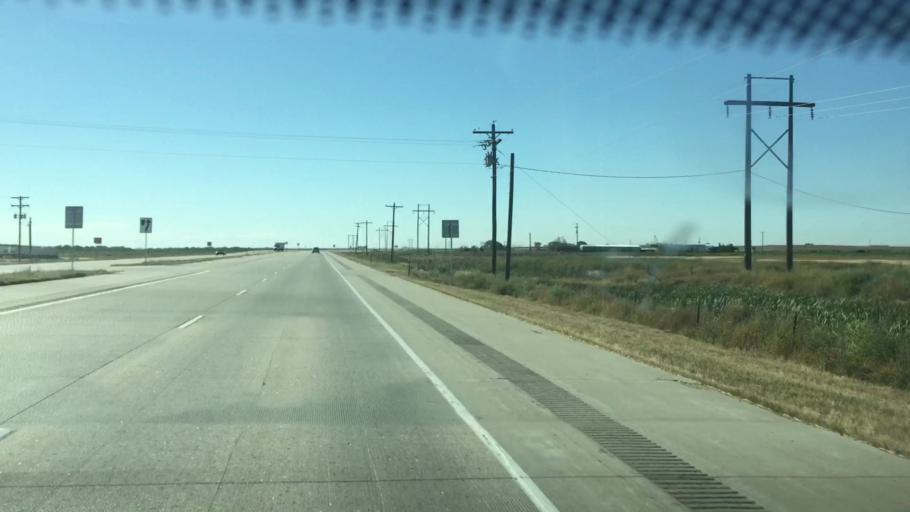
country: US
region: Colorado
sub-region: Prowers County
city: Lamar
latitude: 38.1090
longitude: -102.6905
